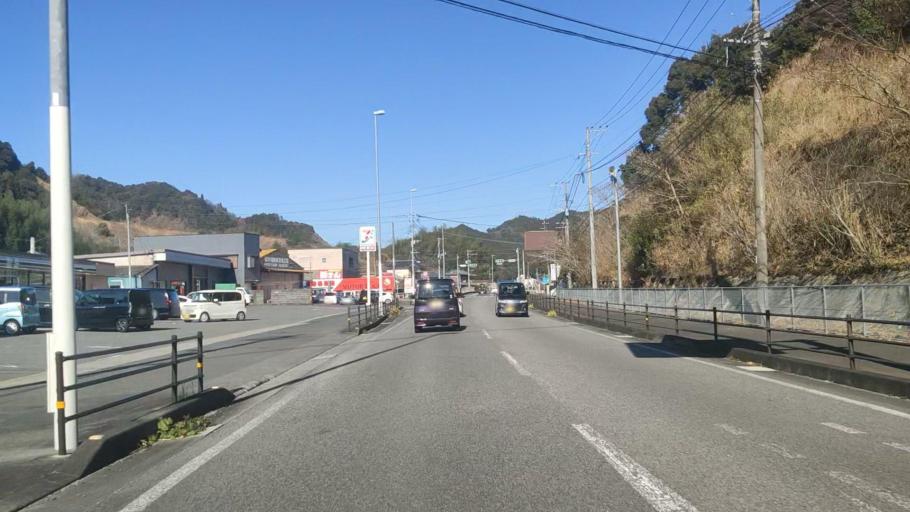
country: JP
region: Oita
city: Saiki
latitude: 32.9670
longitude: 131.8623
